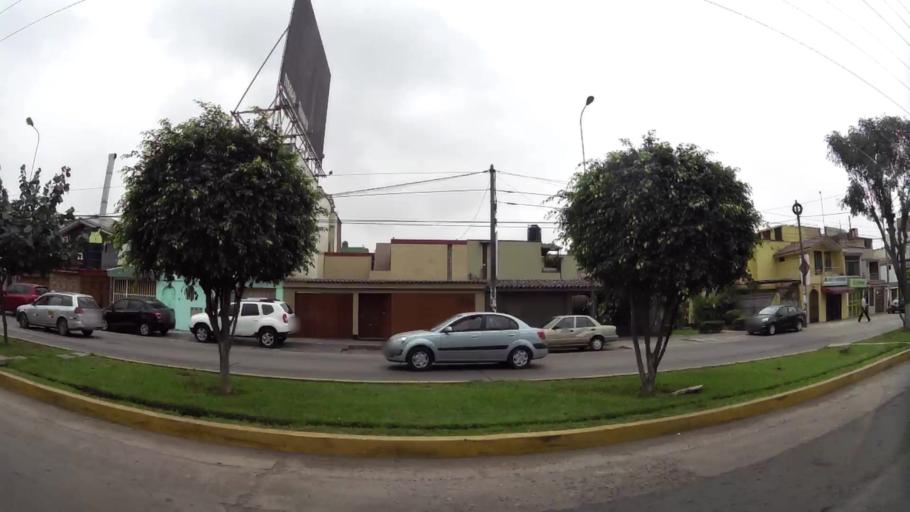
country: PE
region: Lima
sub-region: Lima
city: Surco
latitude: -12.1212
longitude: -77.0044
